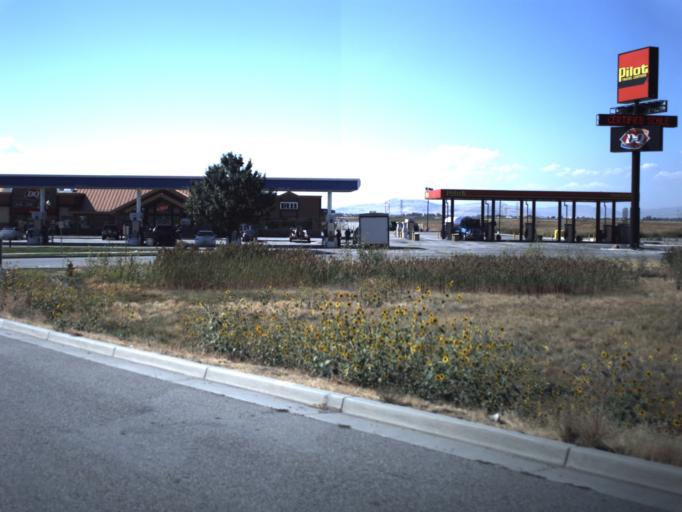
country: US
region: Utah
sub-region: Box Elder County
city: Perry
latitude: 41.4855
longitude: -112.0558
